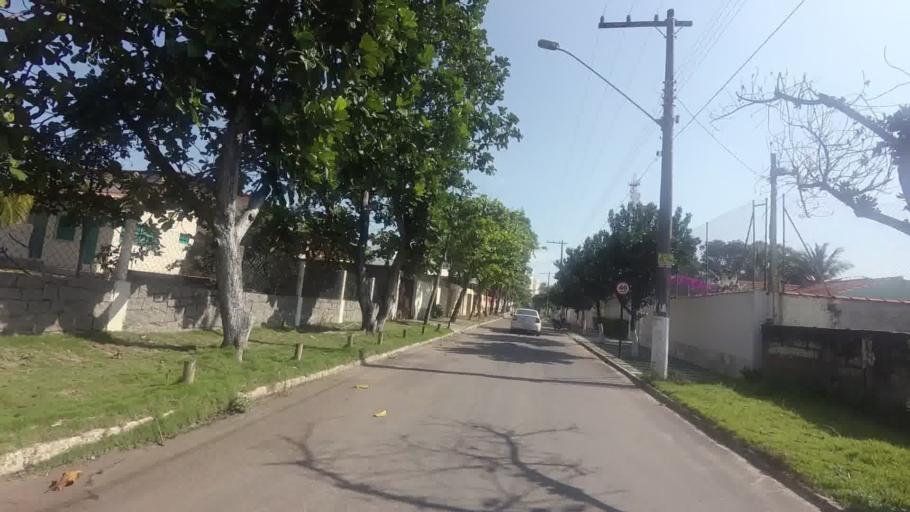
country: BR
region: Espirito Santo
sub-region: Guarapari
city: Guarapari
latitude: -20.7309
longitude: -40.5310
